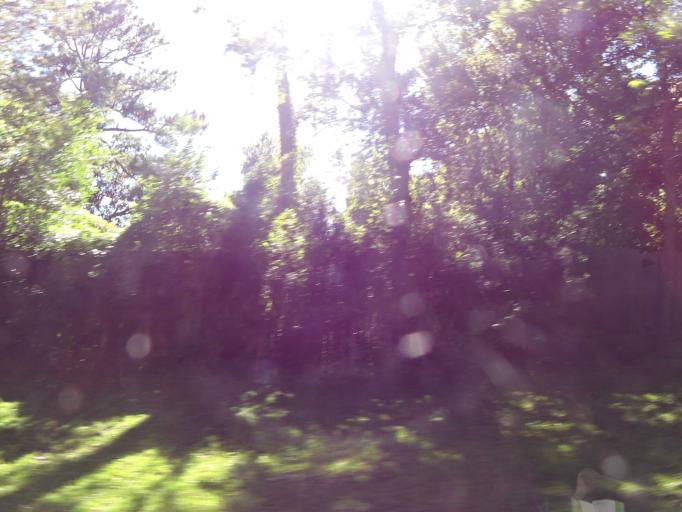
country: US
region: Florida
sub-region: Duval County
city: Jacksonville
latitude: 30.2801
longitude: -81.7241
